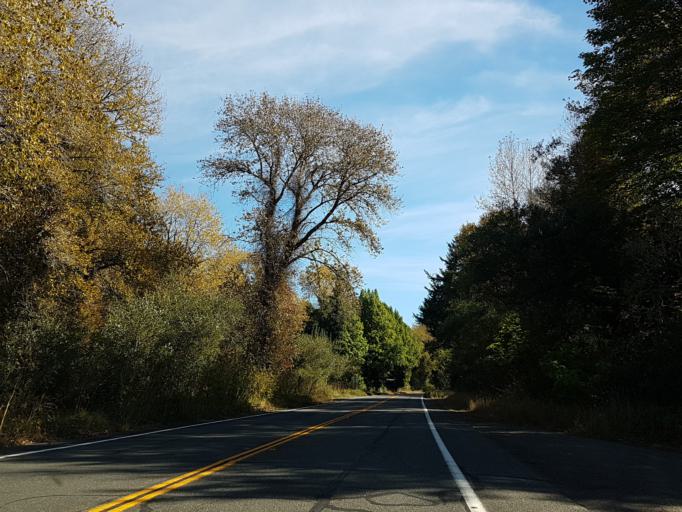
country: US
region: California
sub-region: Humboldt County
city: Rio Dell
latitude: 40.4456
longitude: -123.9885
